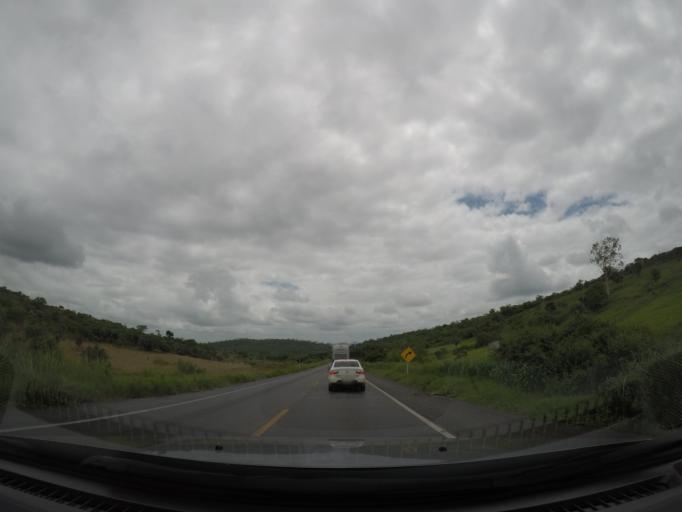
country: BR
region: Bahia
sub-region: Ruy Barbosa
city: Terra Nova
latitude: -12.4507
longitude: -40.6034
